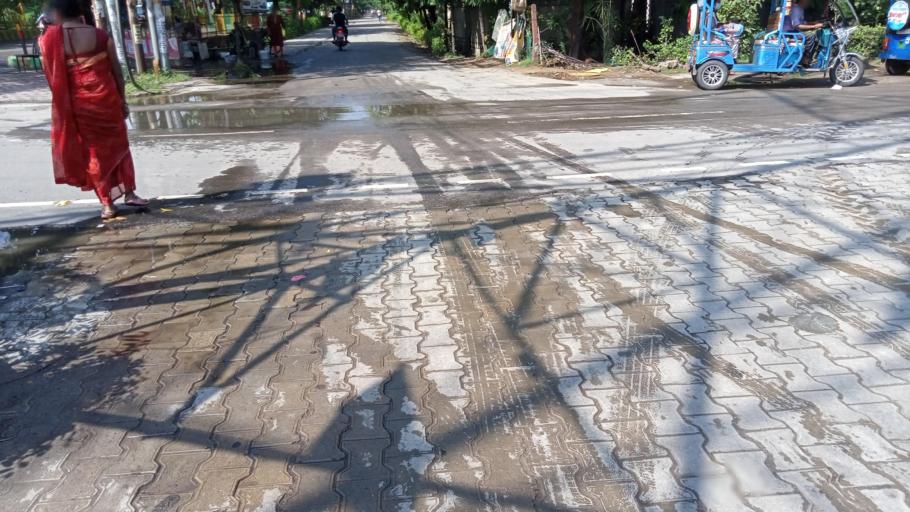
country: IN
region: Uttar Pradesh
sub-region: Ghaziabad
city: Ghaziabad
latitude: 28.6626
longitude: 77.3736
